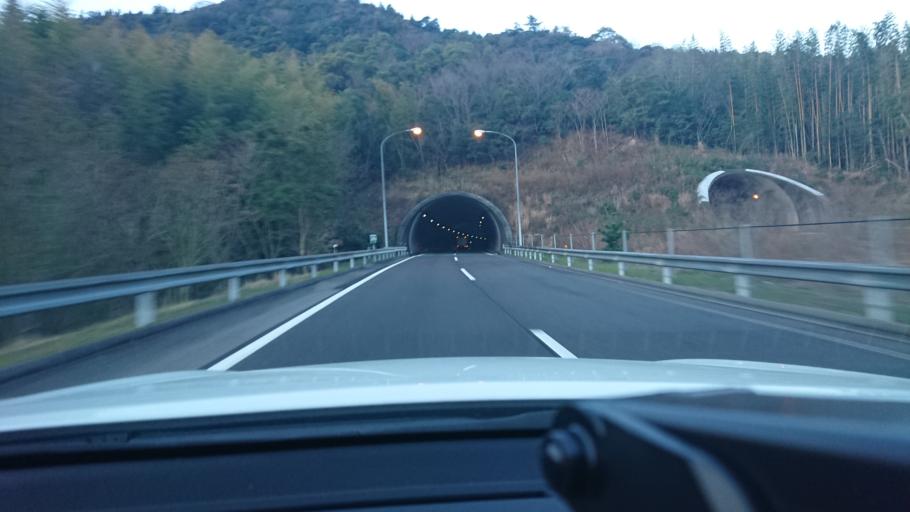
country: JP
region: Kagawa
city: Takamatsu-shi
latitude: 34.2736
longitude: 133.9576
